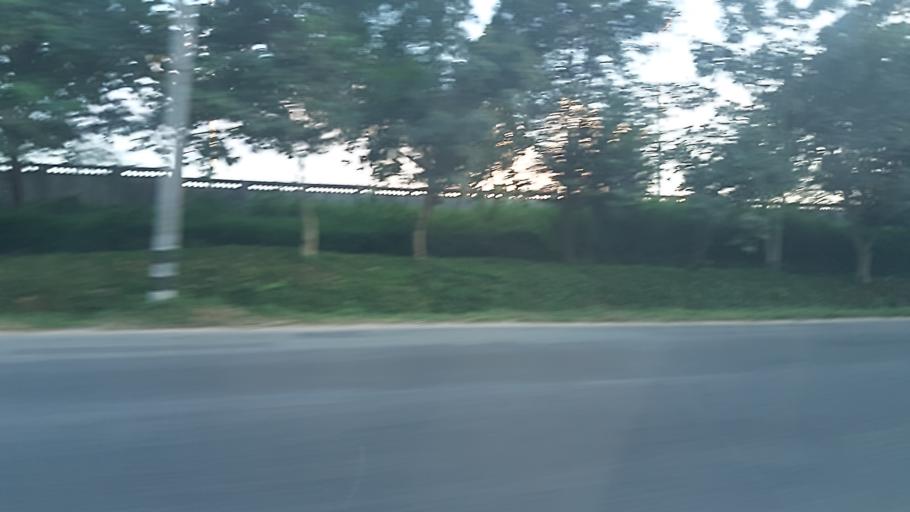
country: MM
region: Yangon
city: Yangon
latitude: 16.9023
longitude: 96.1261
